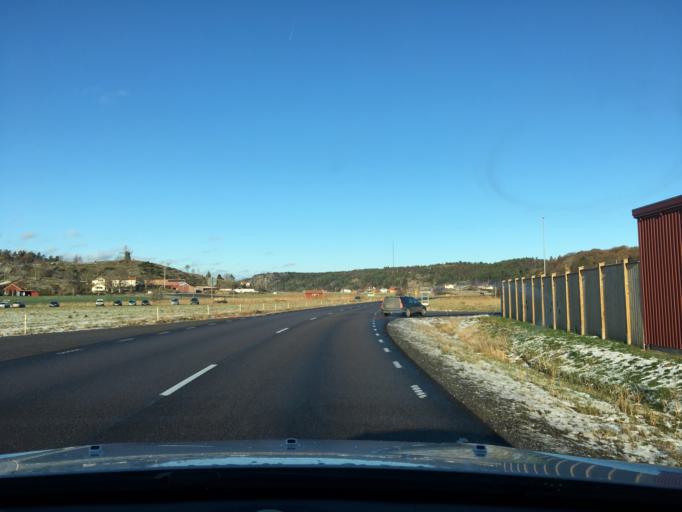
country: SE
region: Vaestra Goetaland
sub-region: Tjorns Kommun
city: Myggenas
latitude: 58.0285
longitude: 11.6563
